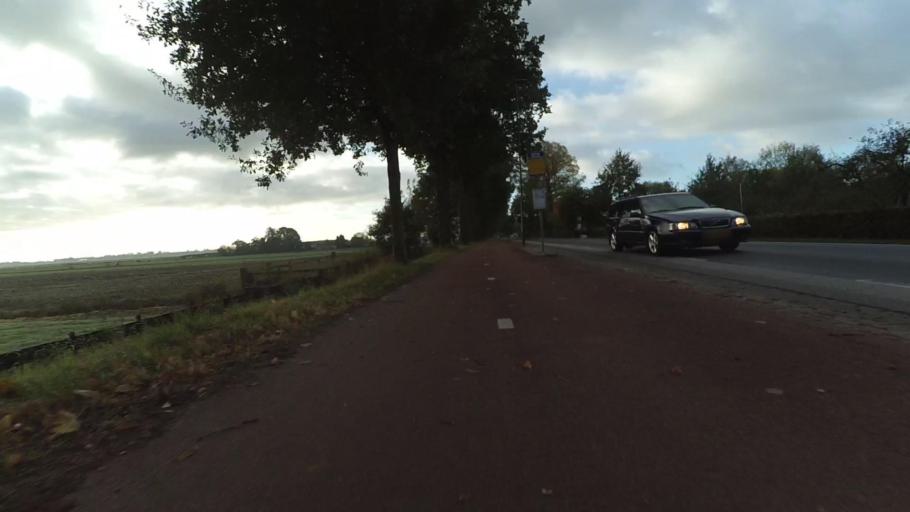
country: NL
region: North Holland
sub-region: Gemeente Blaricum
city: Blaricum
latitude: 52.2437
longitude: 5.2636
